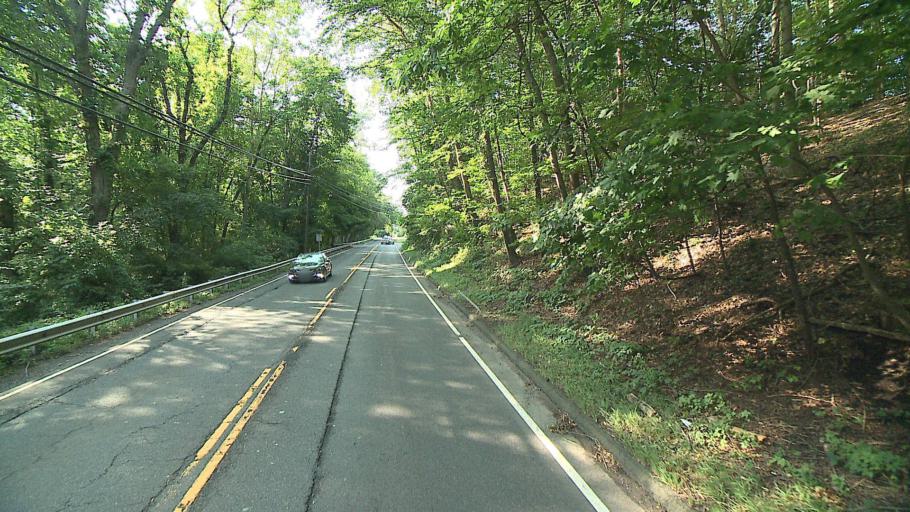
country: US
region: Connecticut
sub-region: Fairfield County
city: Georgetown
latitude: 41.2318
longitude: -73.4272
